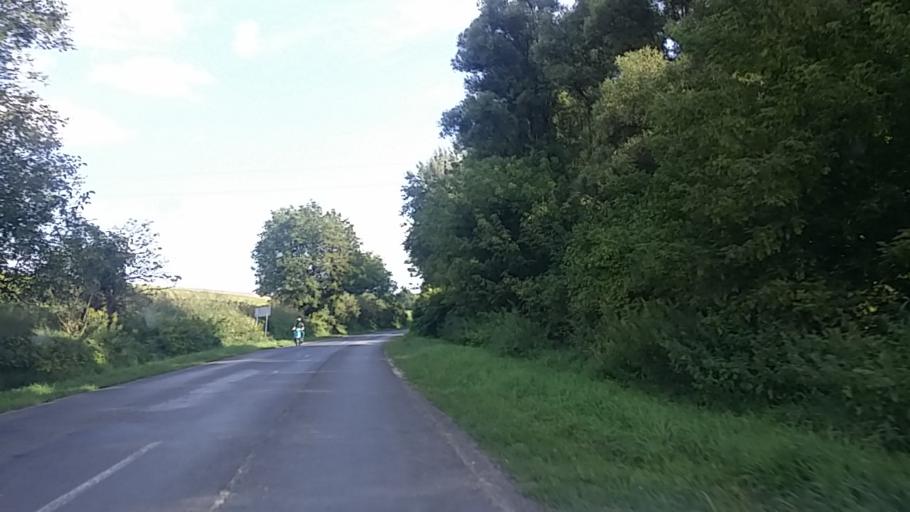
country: HU
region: Tolna
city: Gyonk
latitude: 46.5471
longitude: 18.4913
